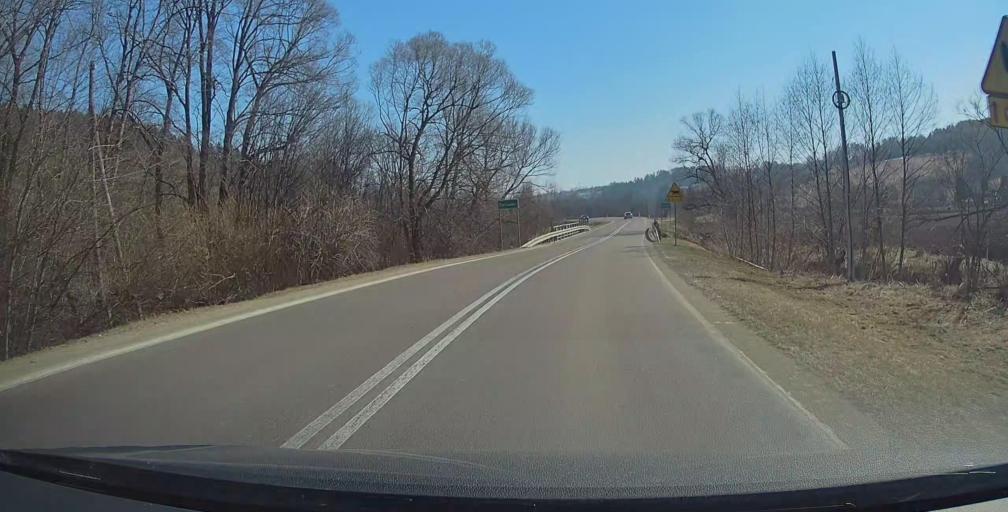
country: PL
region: Subcarpathian Voivodeship
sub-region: Powiat przemyski
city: Bircza
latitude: 49.5870
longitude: 22.5327
